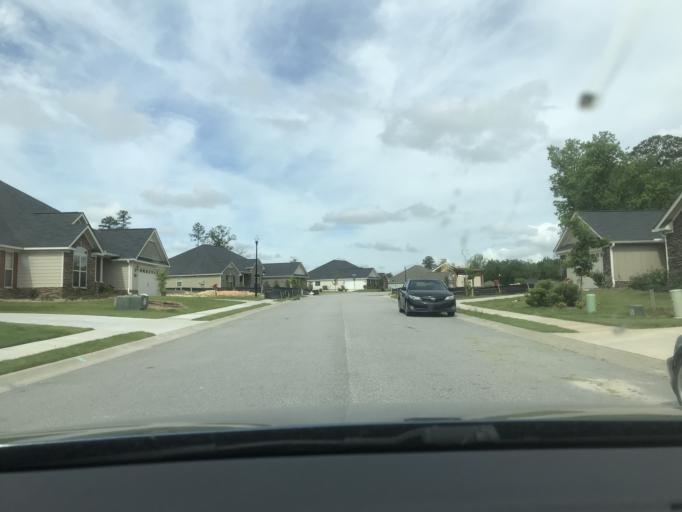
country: US
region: Georgia
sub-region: Columbia County
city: Grovetown
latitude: 33.4464
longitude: -82.1481
